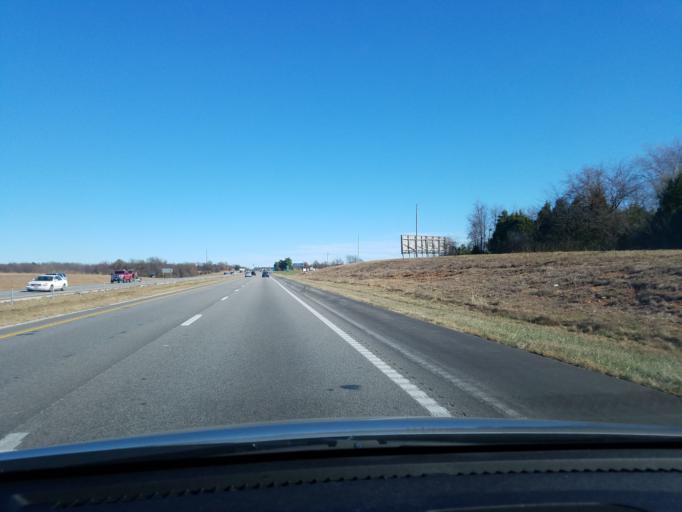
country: US
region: Missouri
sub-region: Greene County
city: Strafford
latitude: 37.2589
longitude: -93.1576
